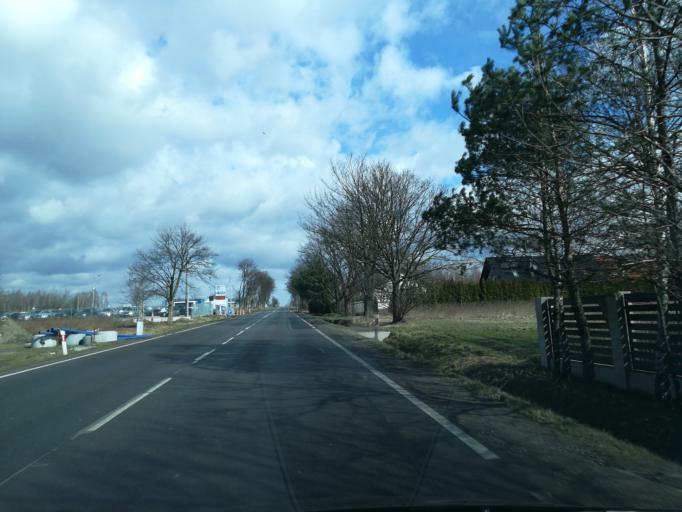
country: PL
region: Lesser Poland Voivodeship
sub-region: Powiat krakowski
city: Kryspinow
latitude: 50.0522
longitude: 19.8006
